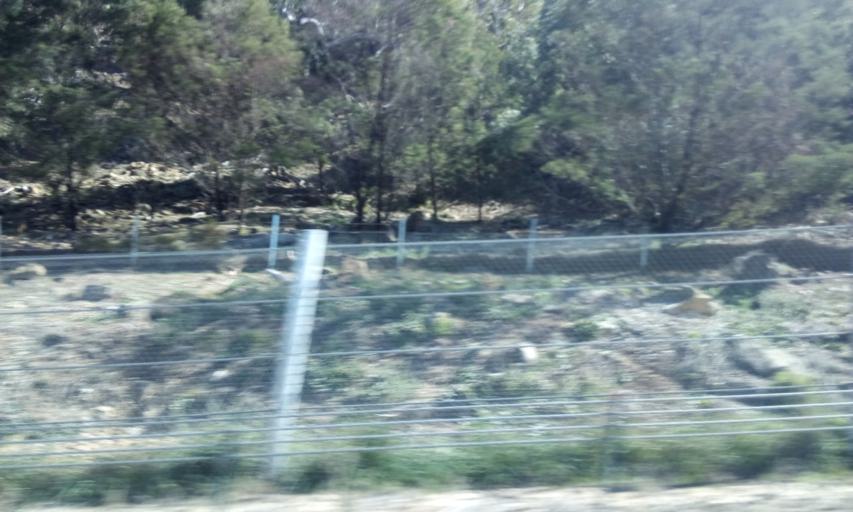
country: AU
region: New South Wales
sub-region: Yass Valley
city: Gundaroo
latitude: -35.0600
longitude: 149.3740
